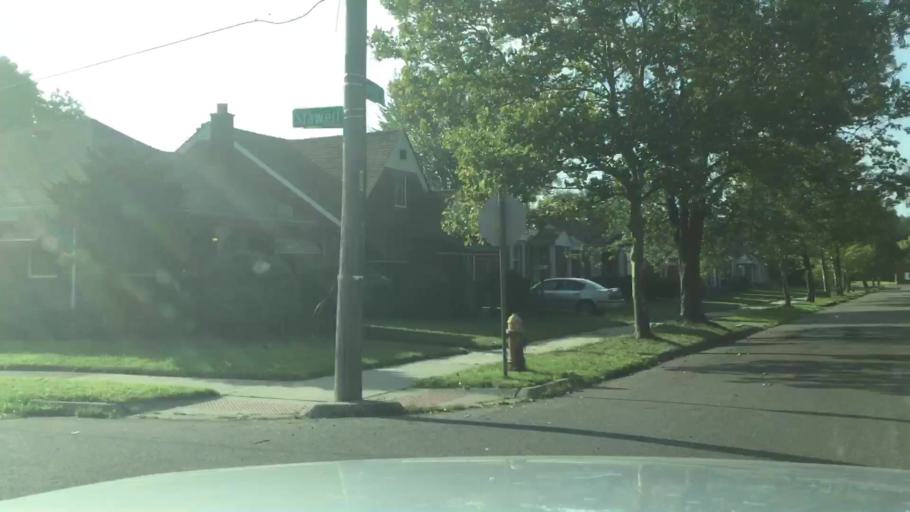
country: US
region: Michigan
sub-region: Wayne County
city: Dearborn
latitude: 42.3609
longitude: -83.1509
